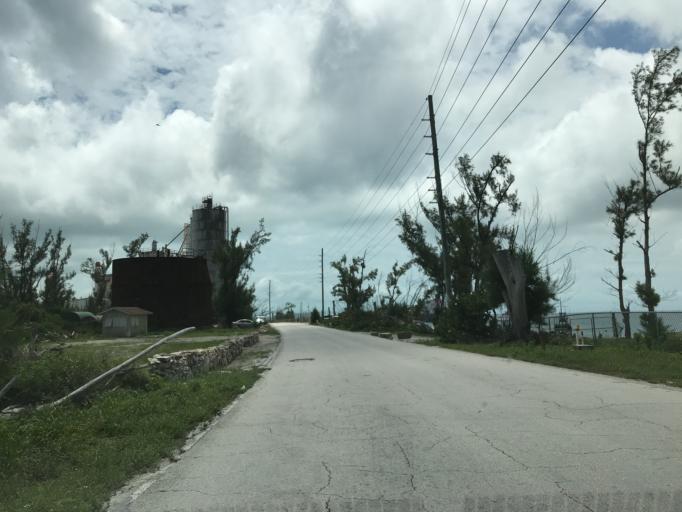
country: BS
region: New Providence
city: Nassau
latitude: 25.0058
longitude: -77.5461
